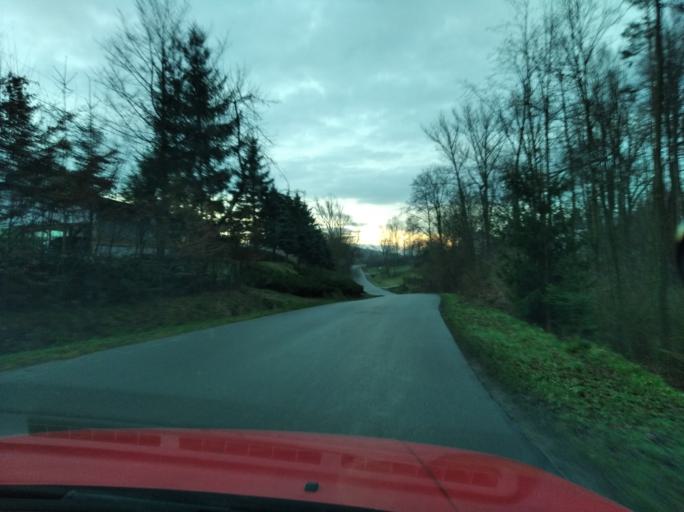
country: PL
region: Subcarpathian Voivodeship
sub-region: Powiat strzyzowski
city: Niebylec
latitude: 49.8718
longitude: 21.8779
